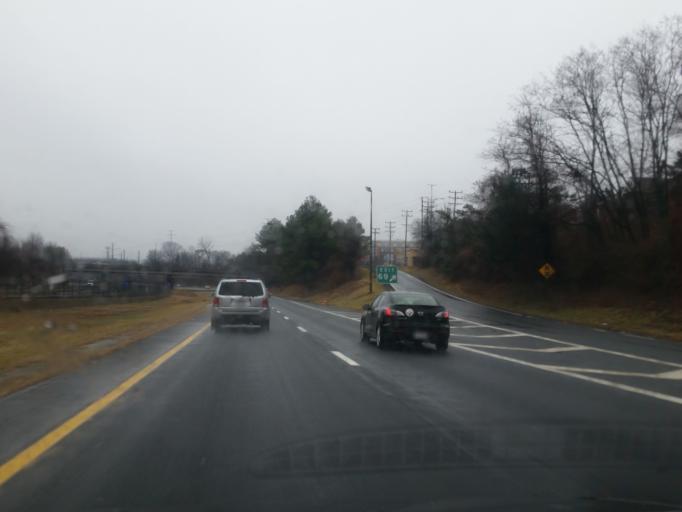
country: US
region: Virginia
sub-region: City of Falls Church
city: Falls Church
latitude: 38.8896
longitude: -77.1641
